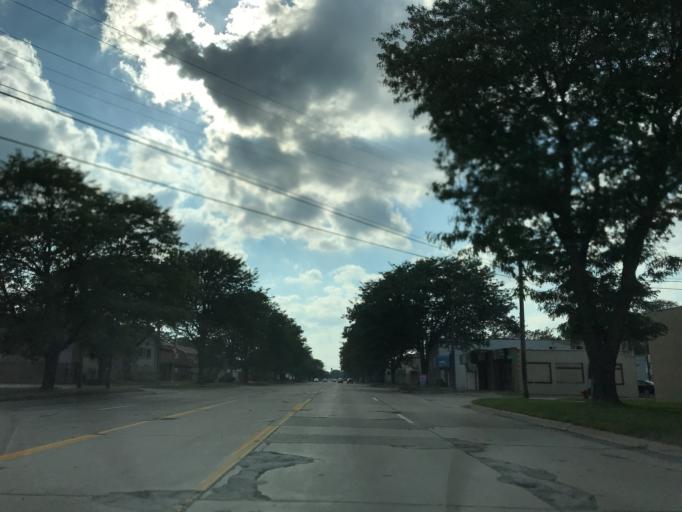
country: US
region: Michigan
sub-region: Wayne County
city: Redford
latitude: 42.3998
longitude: -83.2877
